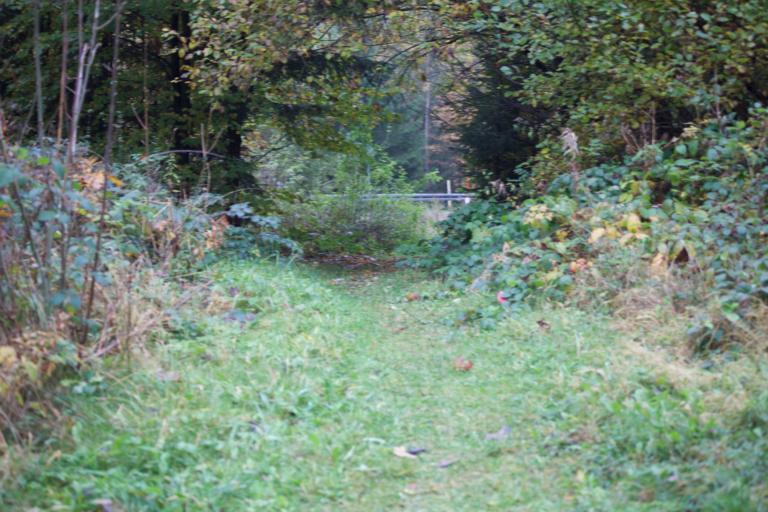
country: DE
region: Lower Saxony
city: Wildemann
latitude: 51.8616
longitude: 10.3104
